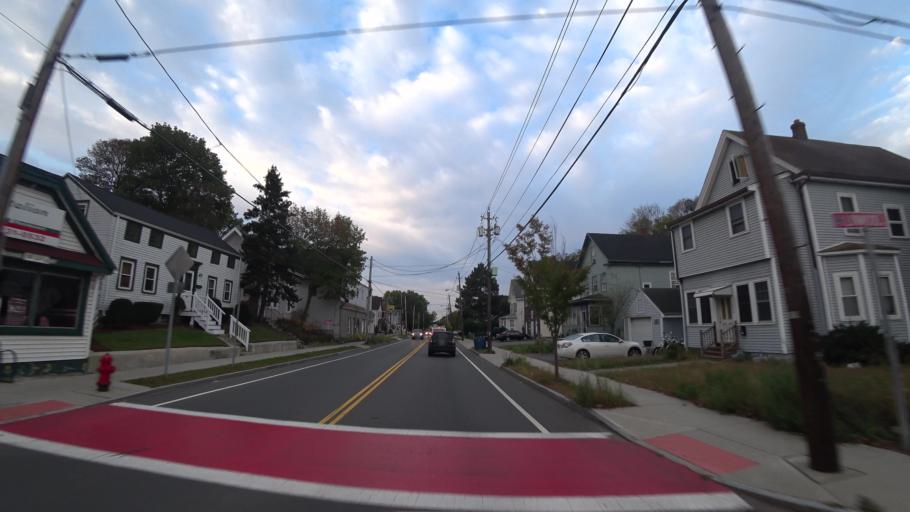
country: US
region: Massachusetts
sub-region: Essex County
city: Saugus
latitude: 42.4470
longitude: -71.0109
